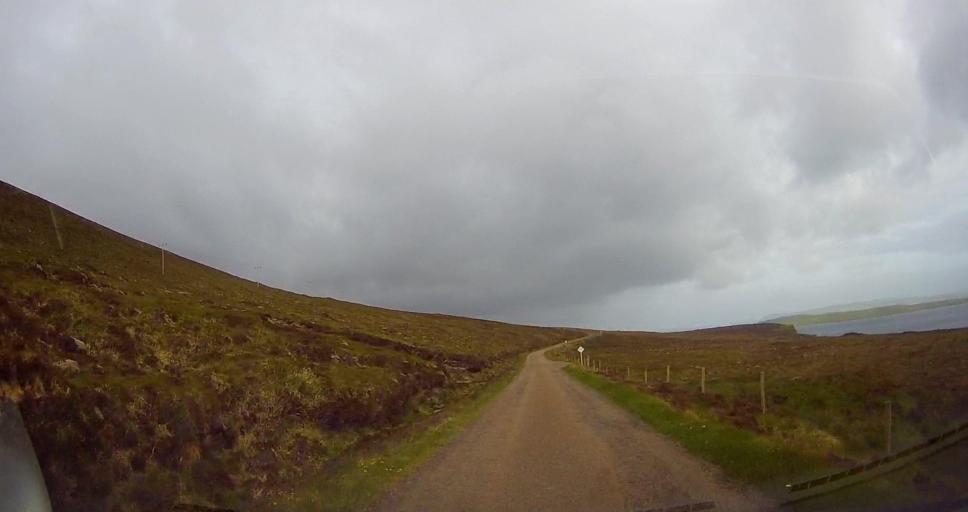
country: GB
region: Scotland
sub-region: Orkney Islands
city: Stromness
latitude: 58.8907
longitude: -3.2587
